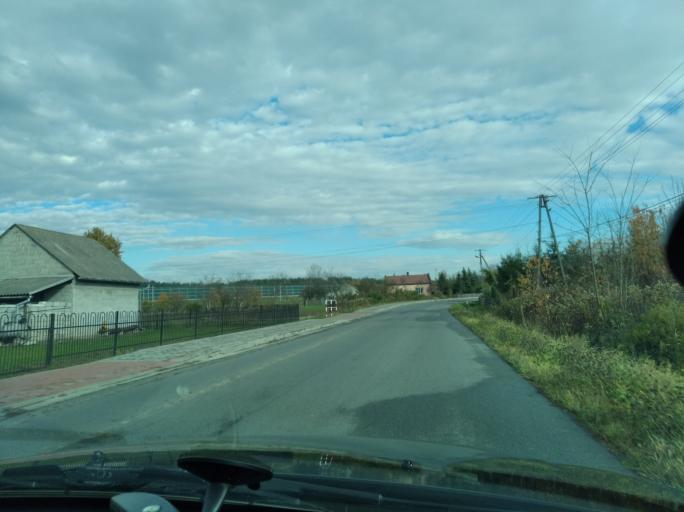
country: PL
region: Subcarpathian Voivodeship
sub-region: Powiat debicki
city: Brzeznica
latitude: 50.0957
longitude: 21.5347
